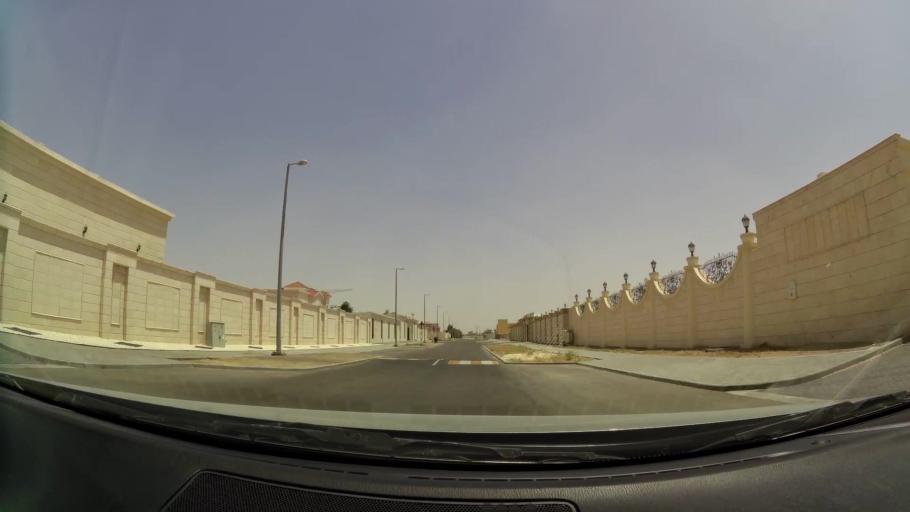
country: AE
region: Abu Dhabi
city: Al Ain
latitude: 24.2510
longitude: 55.7122
